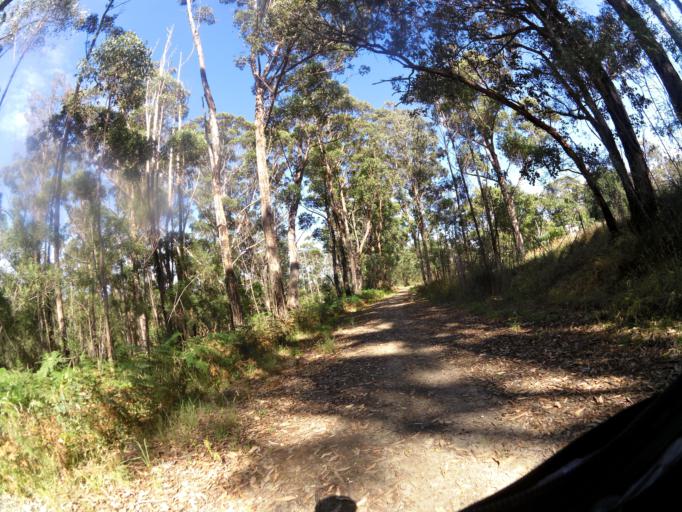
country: AU
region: Victoria
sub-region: East Gippsland
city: Lakes Entrance
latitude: -37.7501
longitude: 148.1831
